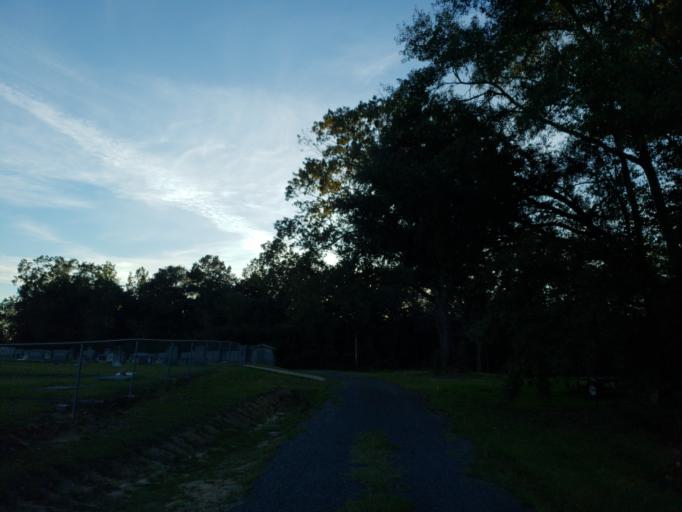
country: US
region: Mississippi
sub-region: Wayne County
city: Belmont
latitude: 31.4326
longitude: -88.4754
